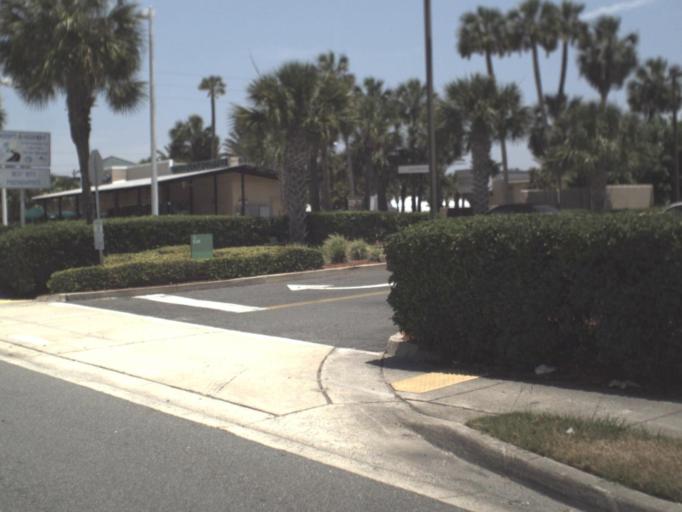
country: US
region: Florida
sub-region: Duval County
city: Atlantic Beach
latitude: 30.3238
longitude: -81.3980
